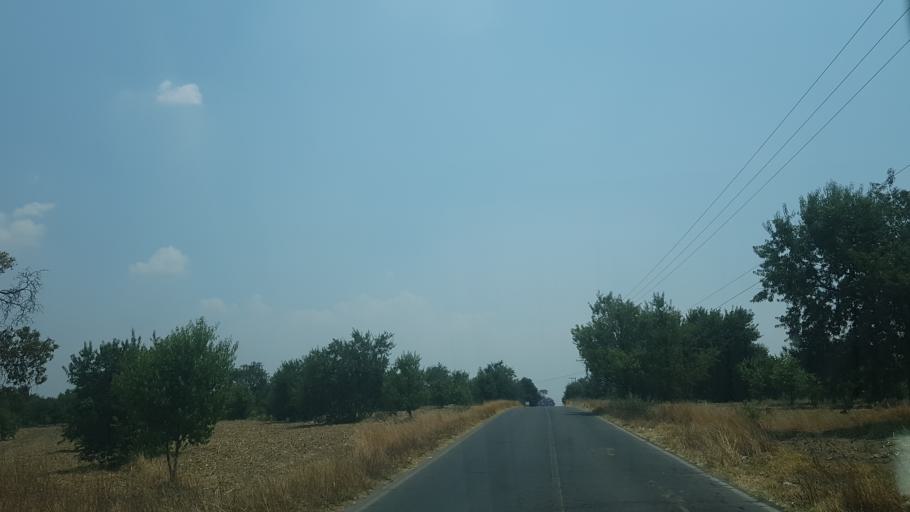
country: MX
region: Puebla
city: San Andres Calpan
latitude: 19.0983
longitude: -98.4232
